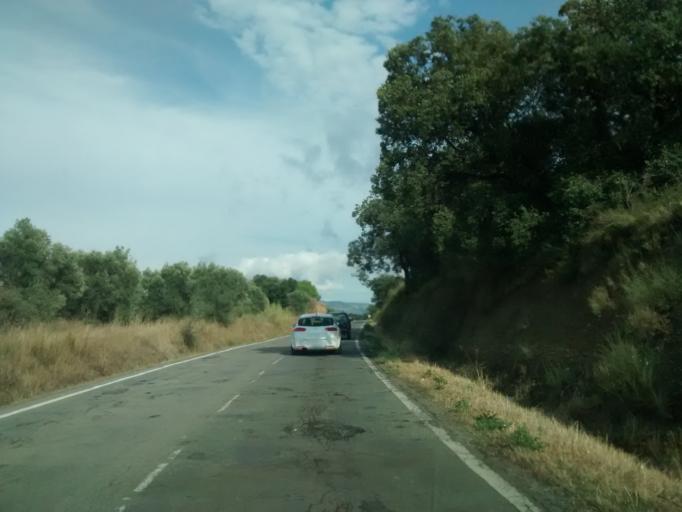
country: ES
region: Aragon
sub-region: Provincia de Huesca
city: Barbastro
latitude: 42.0444
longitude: 0.1415
